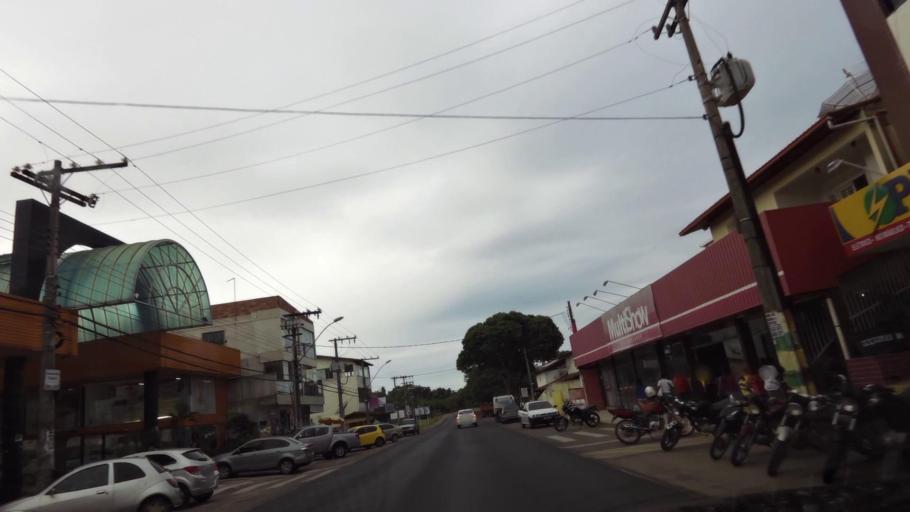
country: BR
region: Espirito Santo
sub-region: Guarapari
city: Guarapari
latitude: -20.7366
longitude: -40.5413
